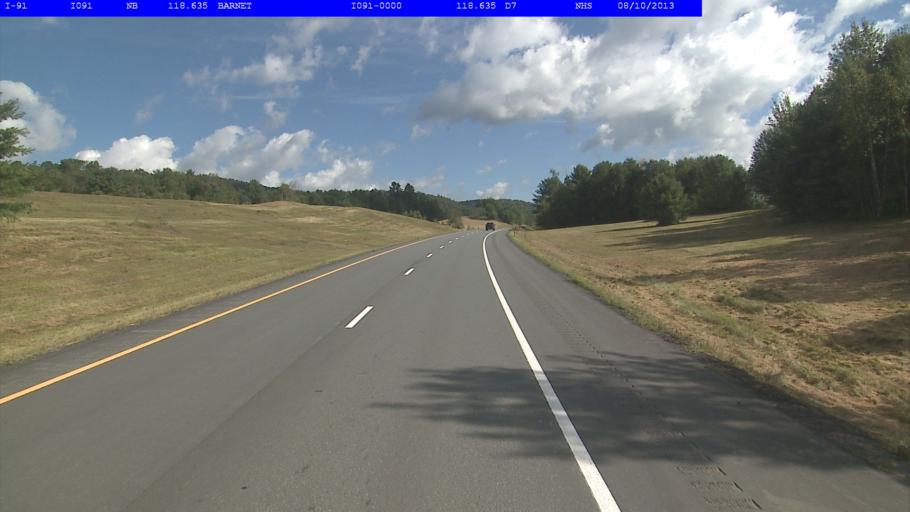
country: US
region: New Hampshire
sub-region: Grafton County
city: Woodsville
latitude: 44.2747
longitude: -72.0718
